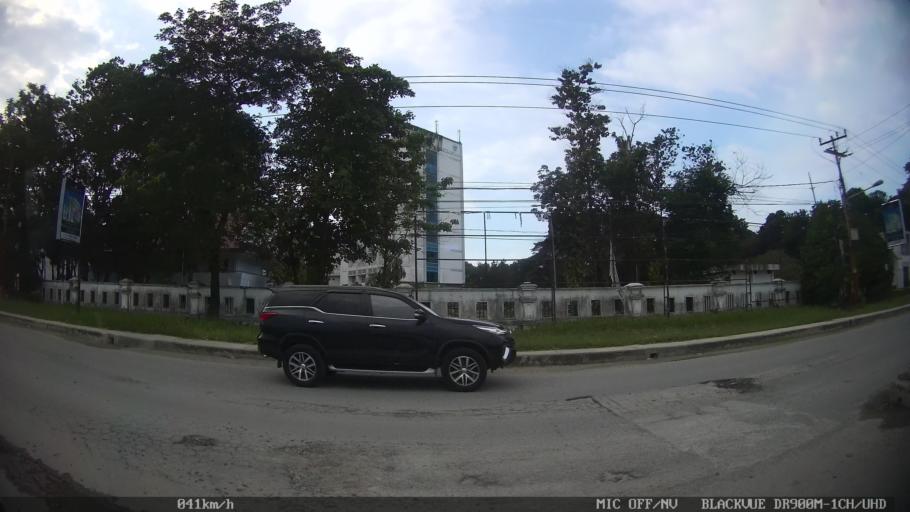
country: ID
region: North Sumatra
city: Medan
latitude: 3.6063
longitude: 98.7159
